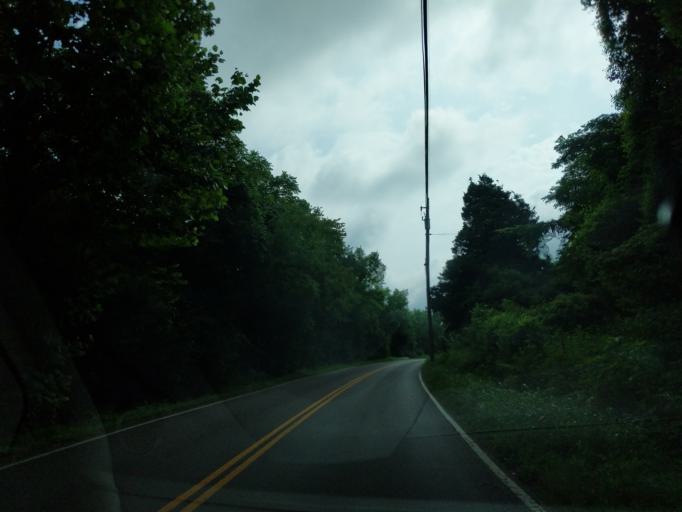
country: US
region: Tennessee
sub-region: Davidson County
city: Lakewood
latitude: 36.1796
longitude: -86.6243
